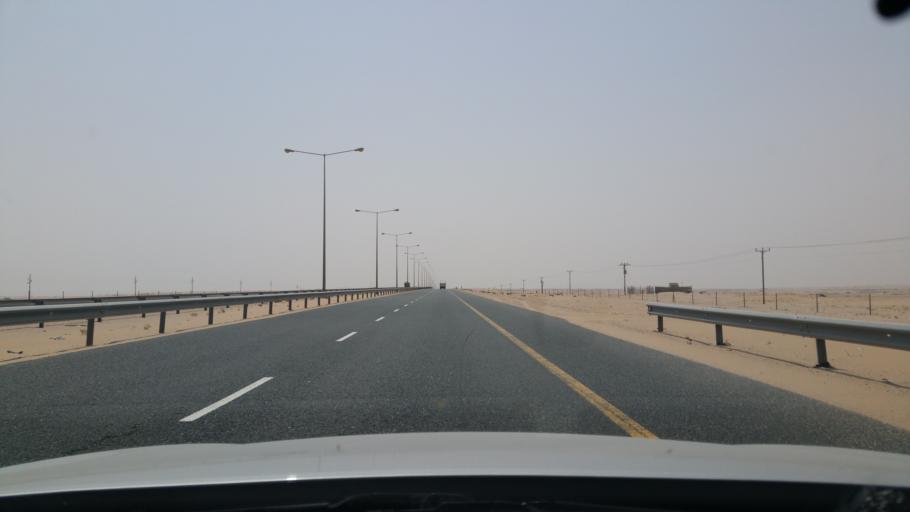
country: QA
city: Umm Bab
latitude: 25.0240
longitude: 50.9055
